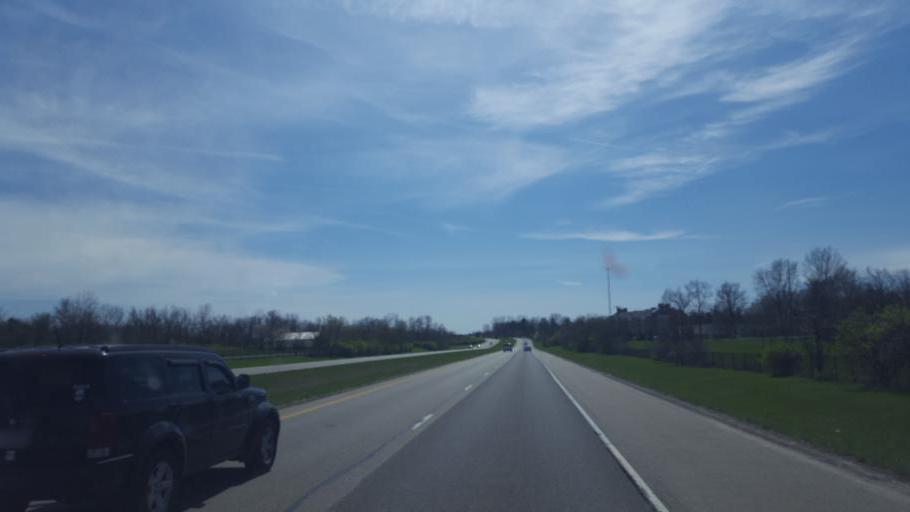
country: US
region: Ohio
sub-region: Delaware County
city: Delaware
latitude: 40.2906
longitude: -83.0631
